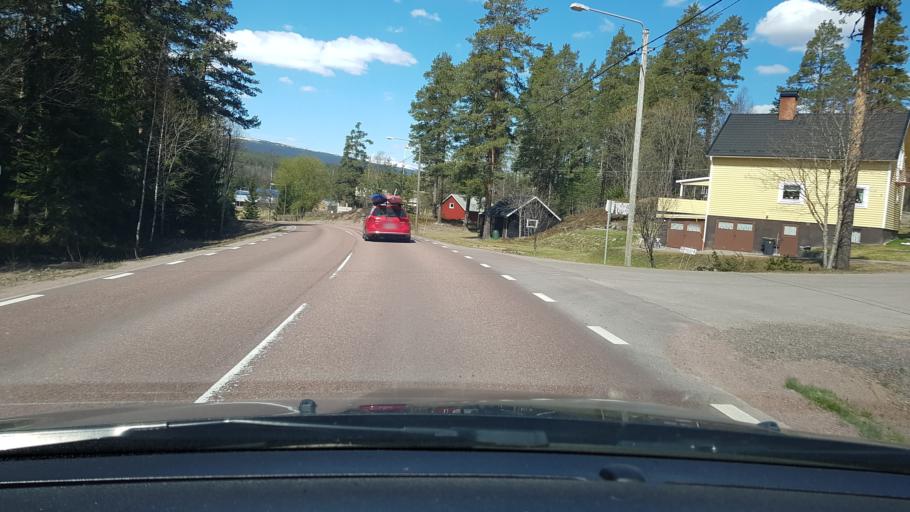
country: SE
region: Dalarna
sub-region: Malung-Saelens kommun
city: Malung
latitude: 61.0662
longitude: 13.3361
